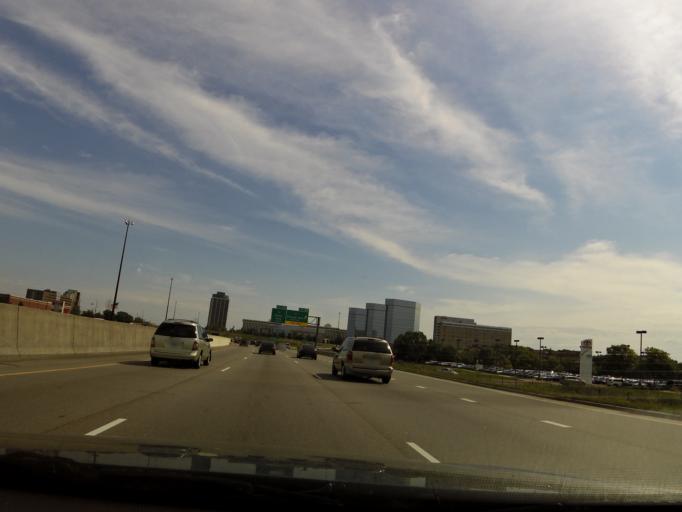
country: US
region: Minnesota
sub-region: Hennepin County
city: Edina
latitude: 44.8577
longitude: -93.3361
